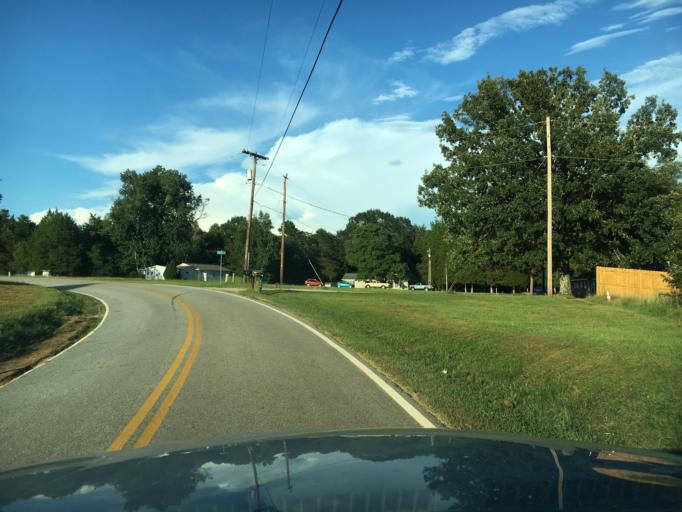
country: US
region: South Carolina
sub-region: Spartanburg County
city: Roebuck
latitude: 34.8876
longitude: -81.9960
